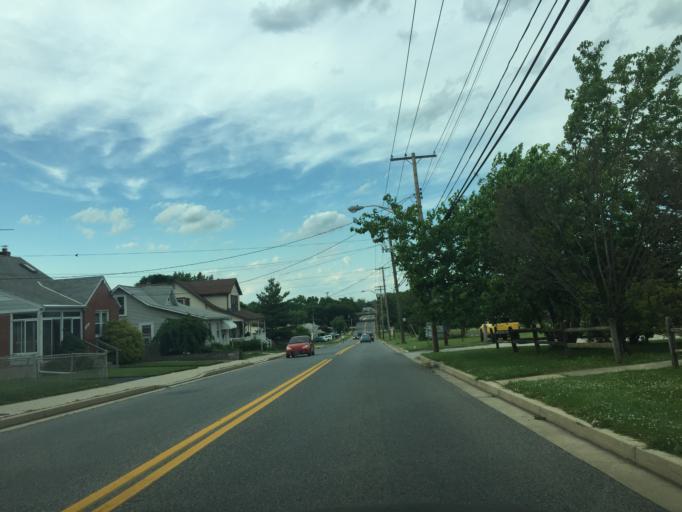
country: US
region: Maryland
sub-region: Baltimore County
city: Essex
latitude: 39.3186
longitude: -76.4744
